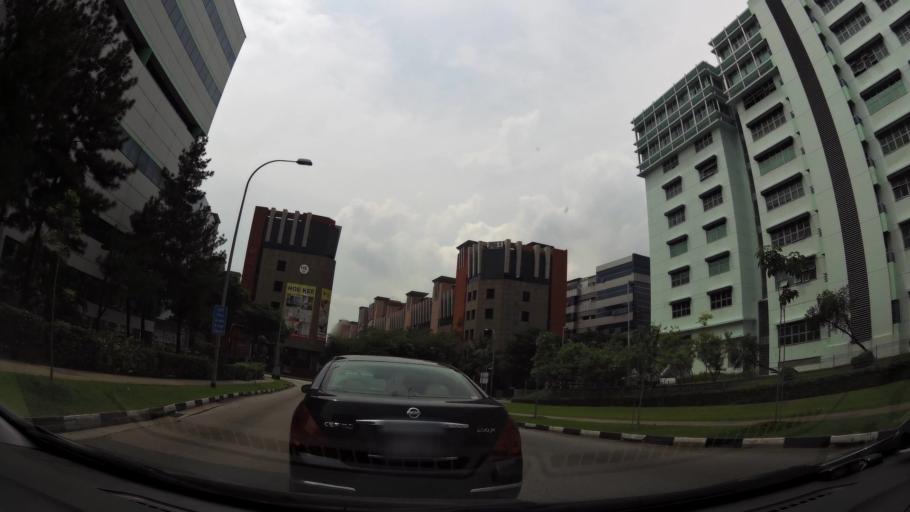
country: SG
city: Singapore
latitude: 1.3364
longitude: 103.9051
